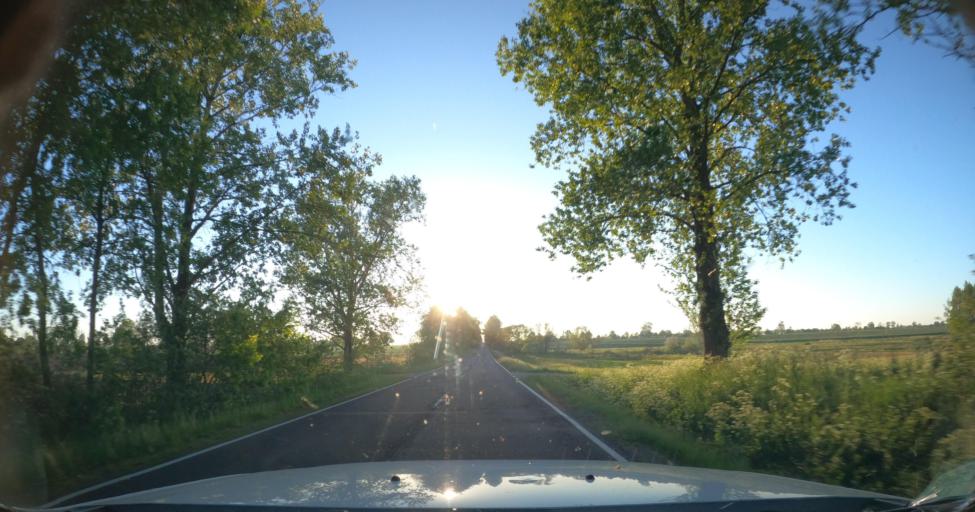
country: PL
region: Pomeranian Voivodeship
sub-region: Powiat slupski
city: Damnica
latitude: 54.4362
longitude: 17.3498
